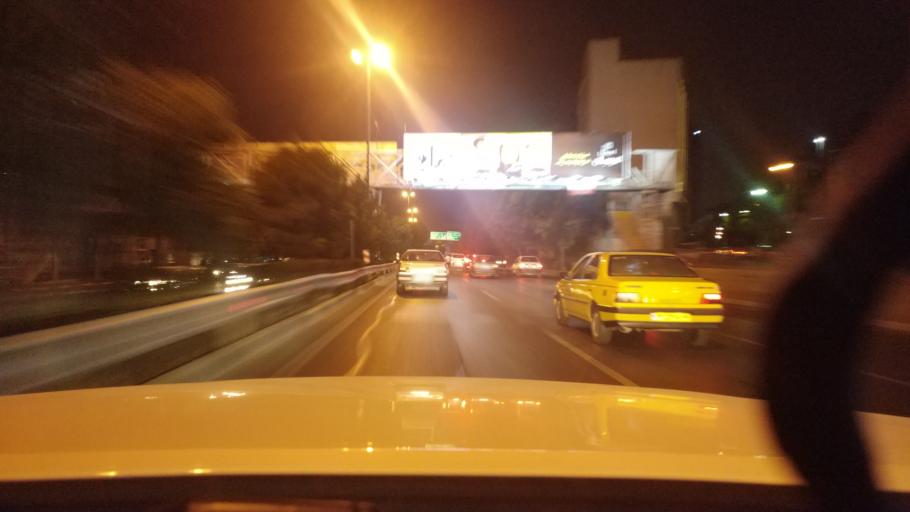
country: IR
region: Tehran
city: Tehran
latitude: 35.7371
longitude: 51.3191
